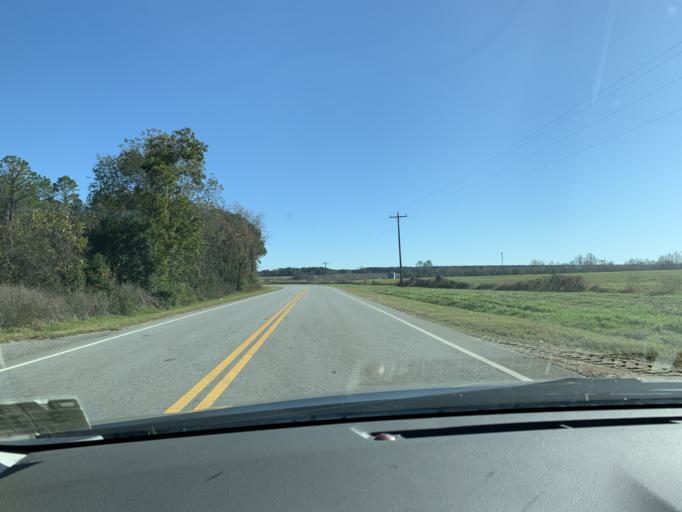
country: US
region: Georgia
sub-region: Ben Hill County
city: Fitzgerald
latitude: 31.7131
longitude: -83.1889
